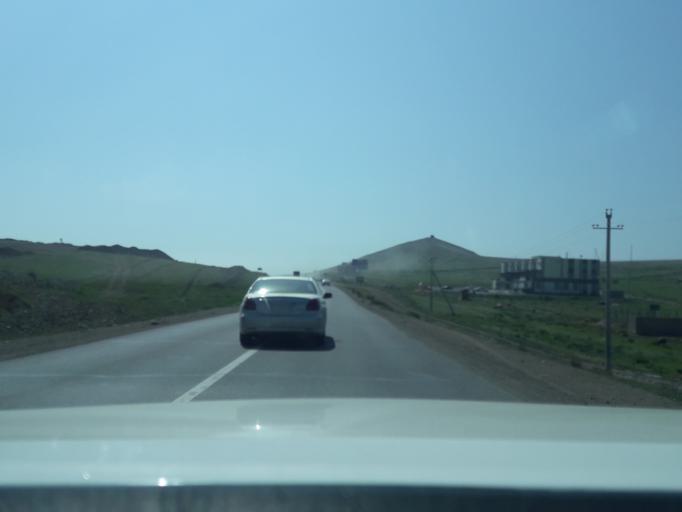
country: MN
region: Ulaanbaatar
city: Ulaanbaatar
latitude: 47.7921
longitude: 106.7455
